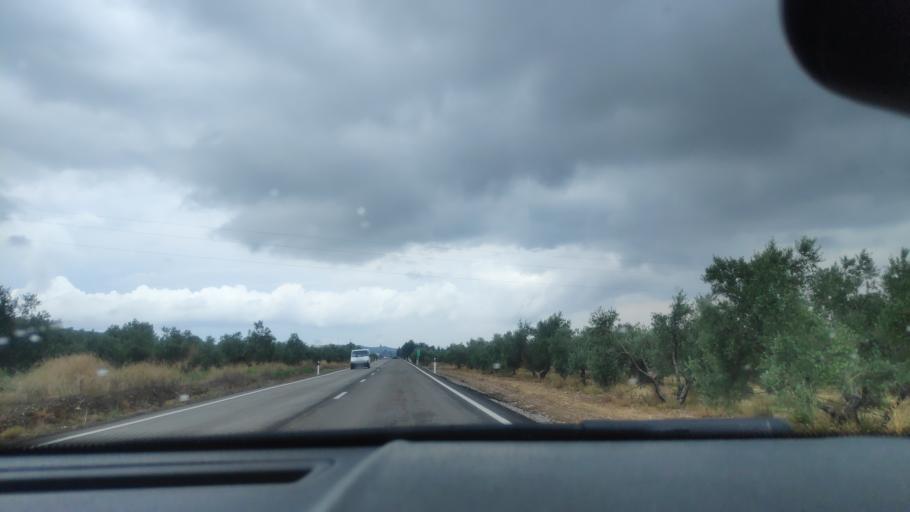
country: ES
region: Andalusia
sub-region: Provincia de Jaen
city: Jabalquinto
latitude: 38.0318
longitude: -3.7631
